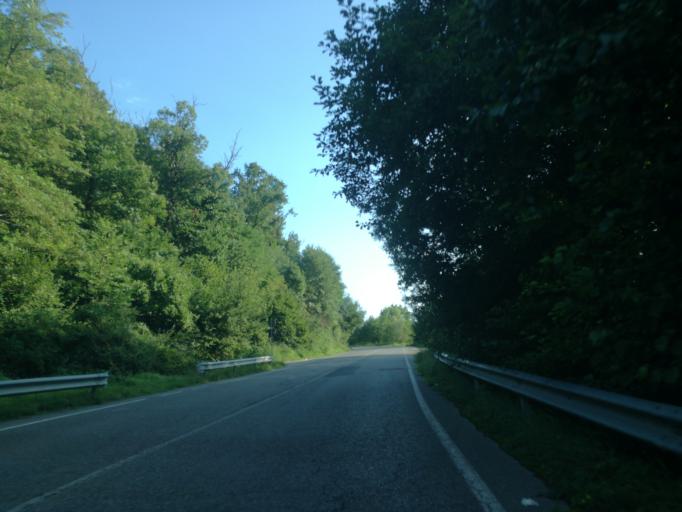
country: IT
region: Lombardy
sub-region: Provincia di Bergamo
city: Cisano Bergamasco
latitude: 45.7479
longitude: 9.4611
